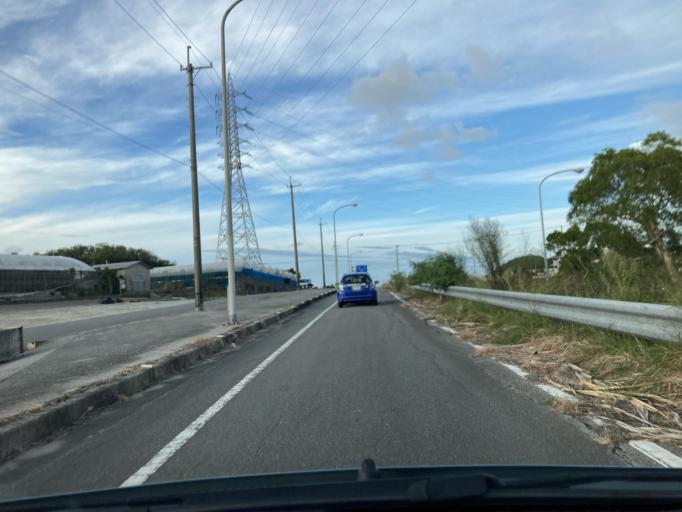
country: JP
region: Okinawa
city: Tomigusuku
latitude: 26.1721
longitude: 127.7267
